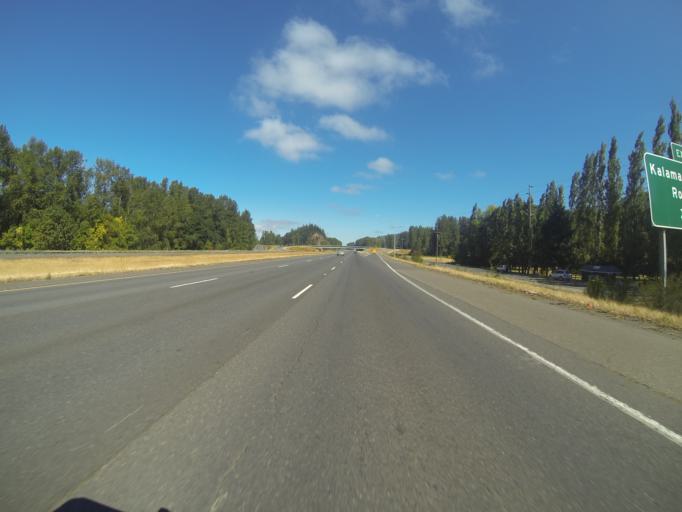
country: US
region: Washington
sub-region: Cowlitz County
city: Kalama
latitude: 46.0373
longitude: -122.8575
